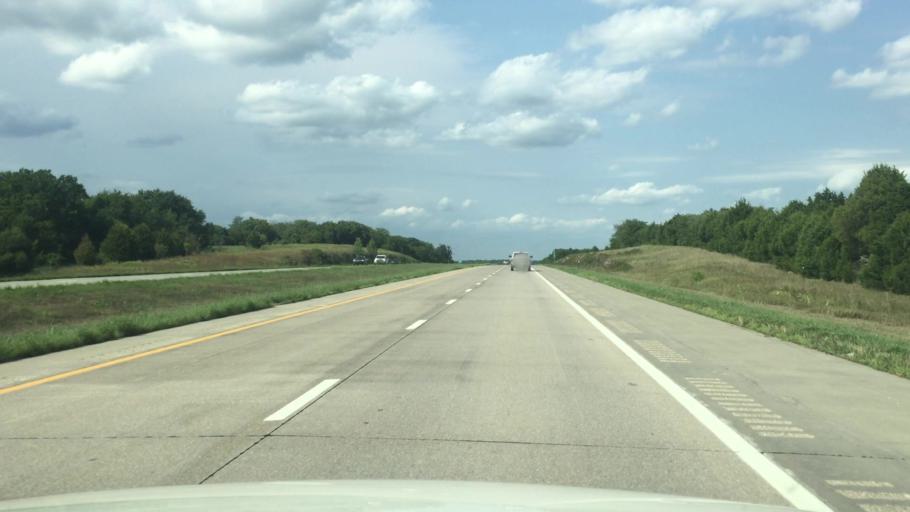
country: US
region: Kansas
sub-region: Miami County
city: Louisburg
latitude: 38.5816
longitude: -94.6952
